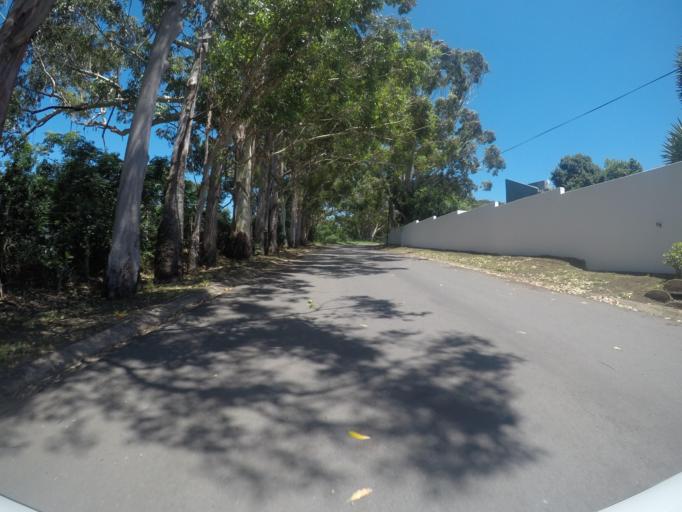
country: ZA
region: Eastern Cape
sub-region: Buffalo City Metropolitan Municipality
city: East London
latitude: -32.9343
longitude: 28.0054
